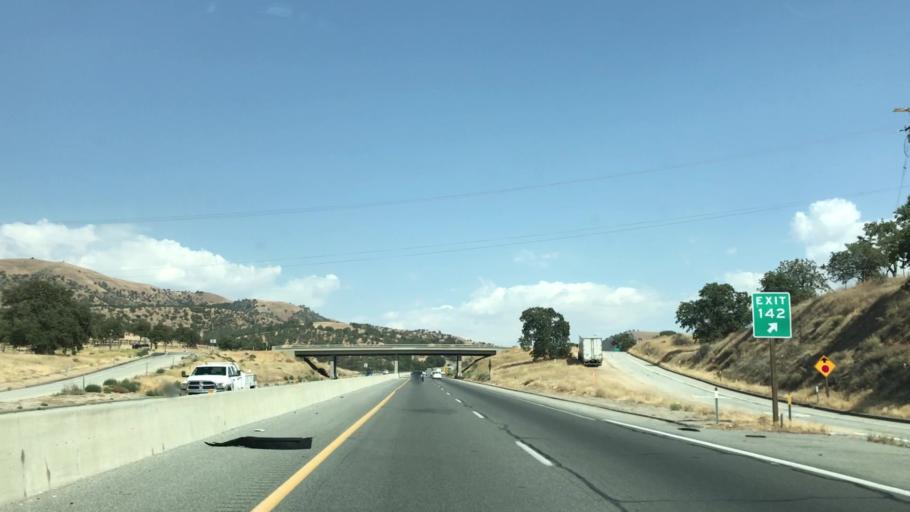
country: US
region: California
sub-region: Kern County
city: Golden Hills
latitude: 35.2009
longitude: -118.5240
